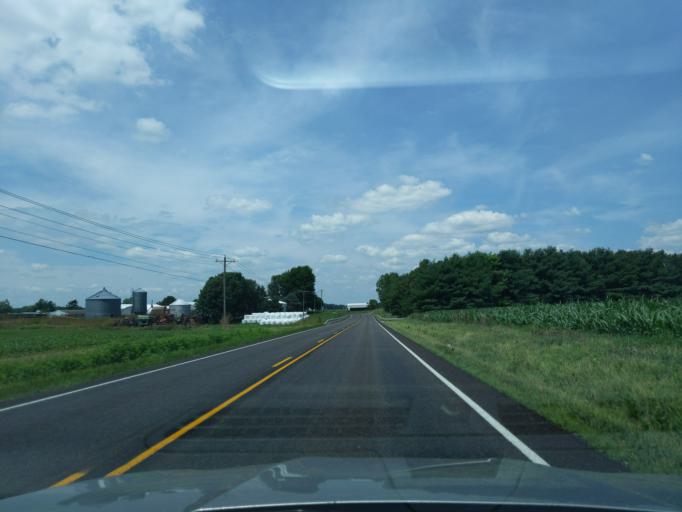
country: US
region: Indiana
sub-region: Ripley County
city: Osgood
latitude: 39.2260
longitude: -85.3363
